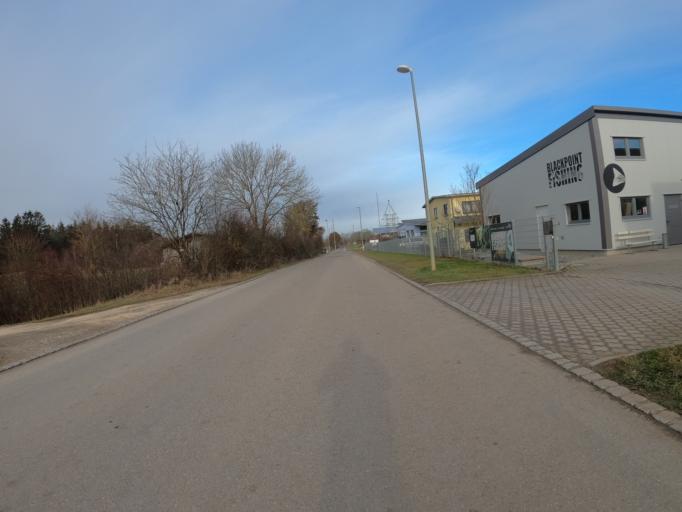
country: DE
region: Bavaria
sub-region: Swabia
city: Nersingen
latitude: 48.4191
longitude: 10.1740
